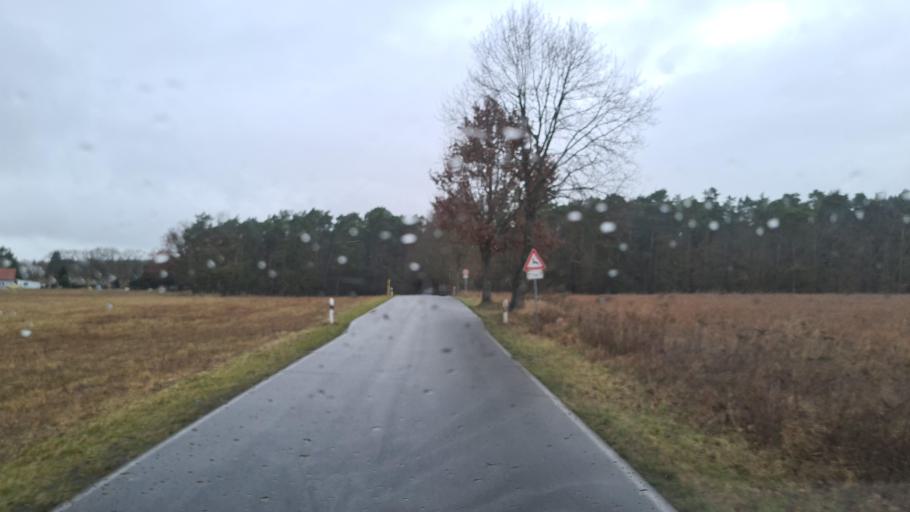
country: DE
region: Brandenburg
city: Oranienburg
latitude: 52.8827
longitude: 13.2102
